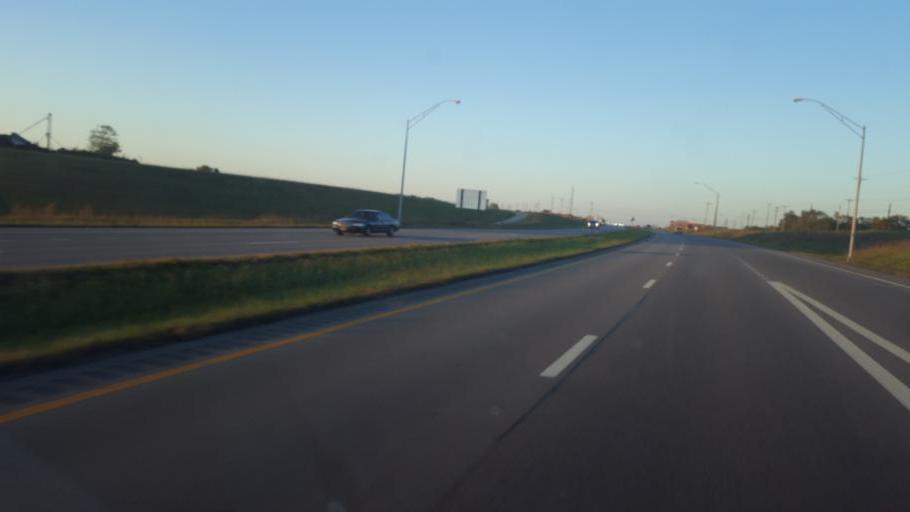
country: US
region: Ohio
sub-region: Pike County
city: Piketon
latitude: 39.0516
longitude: -83.0210
